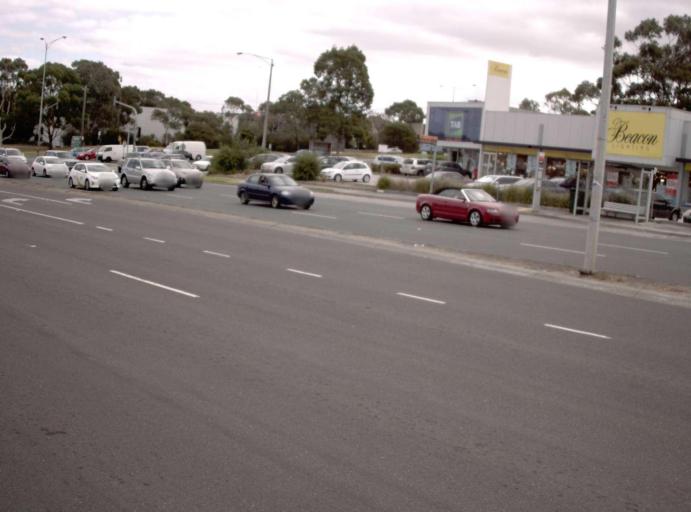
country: AU
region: Victoria
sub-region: Knox
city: Scoresby
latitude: -37.8983
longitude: 145.2331
